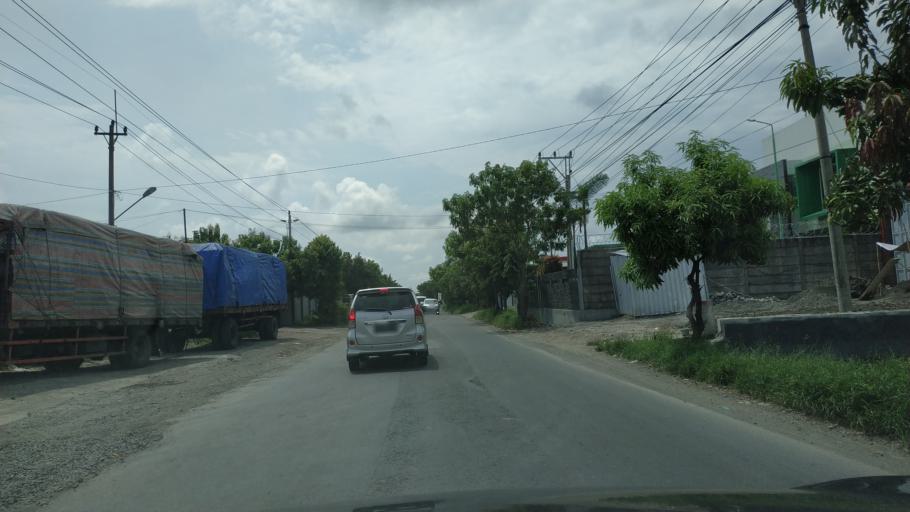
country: ID
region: Central Java
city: Adiwerna
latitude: -6.9267
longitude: 109.1258
